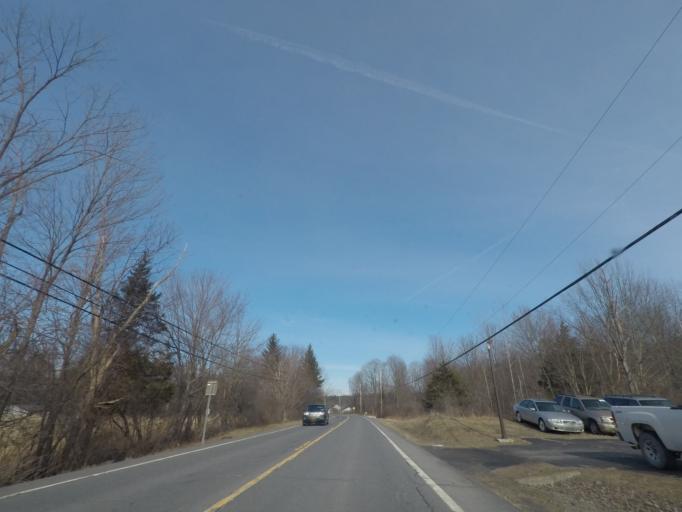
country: US
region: New York
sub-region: Rensselaer County
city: Nassau
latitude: 42.4995
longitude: -73.6189
